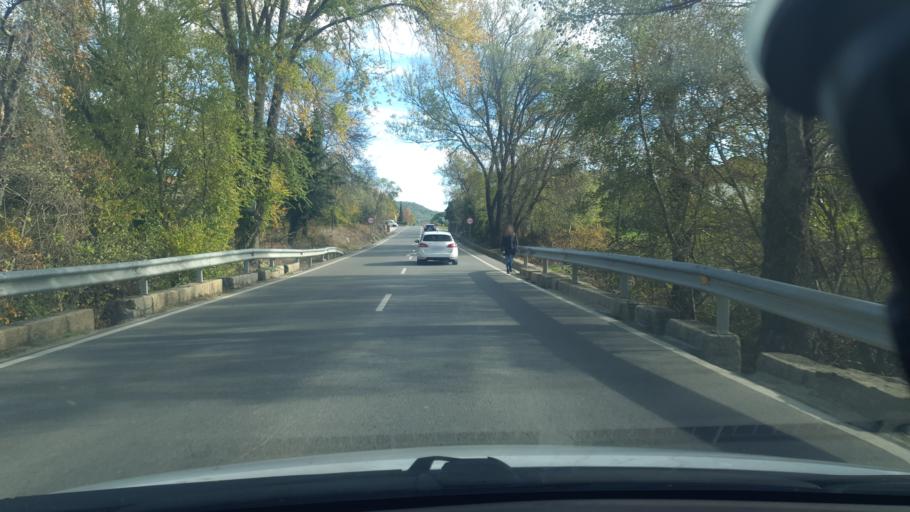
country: ES
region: Castille and Leon
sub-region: Provincia de Avila
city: La Adrada
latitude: 40.3071
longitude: -4.6493
